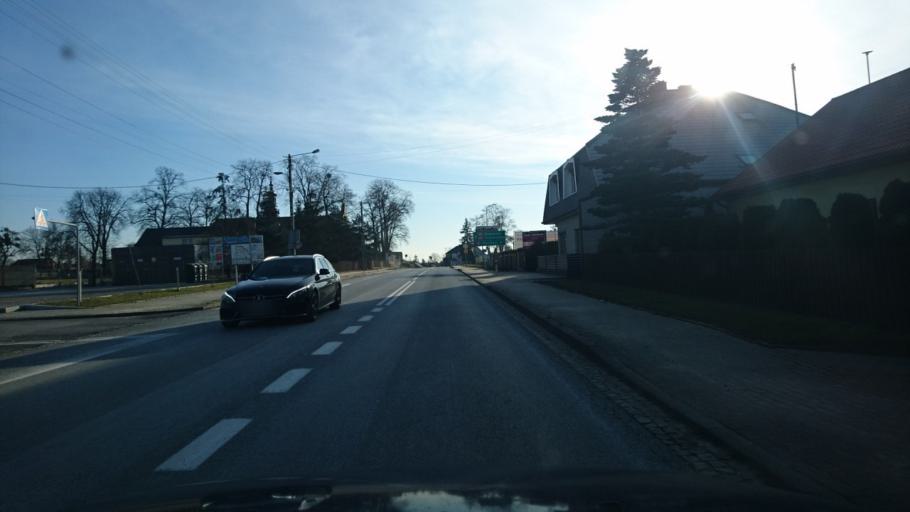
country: PL
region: Opole Voivodeship
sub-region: Powiat oleski
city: Dalachow
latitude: 51.0404
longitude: 18.5976
